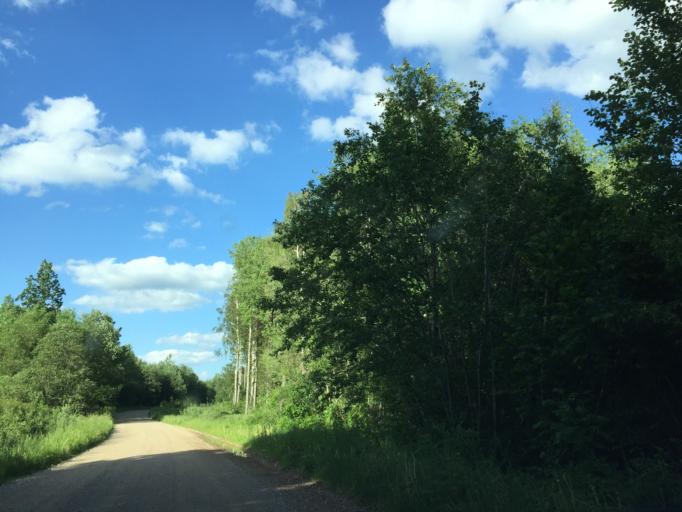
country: LV
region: Kandava
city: Kandava
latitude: 56.8359
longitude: 22.7517
